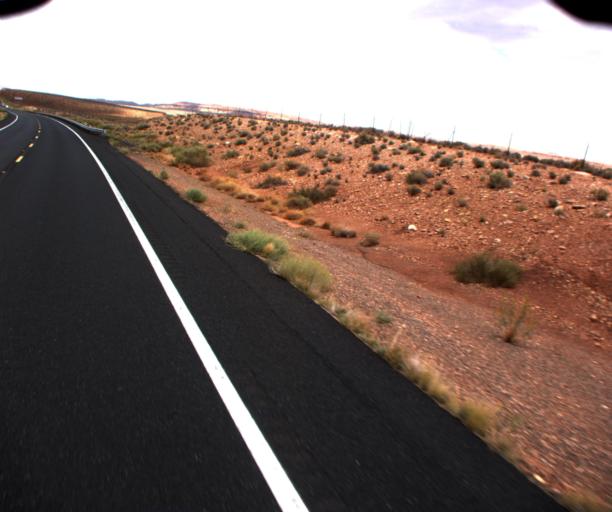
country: US
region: Arizona
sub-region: Coconino County
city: Tuba City
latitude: 35.9073
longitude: -111.5509
